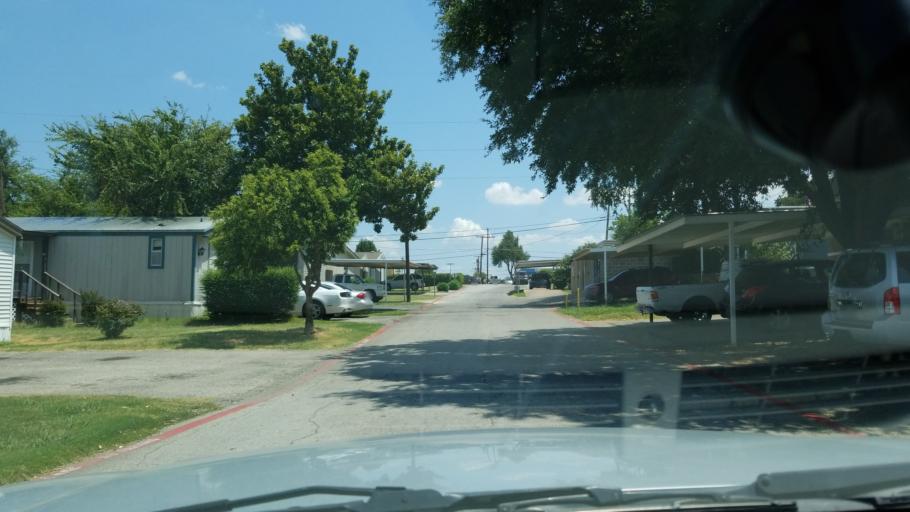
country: US
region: Texas
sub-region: Dallas County
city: Irving
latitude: 32.8260
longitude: -96.9950
